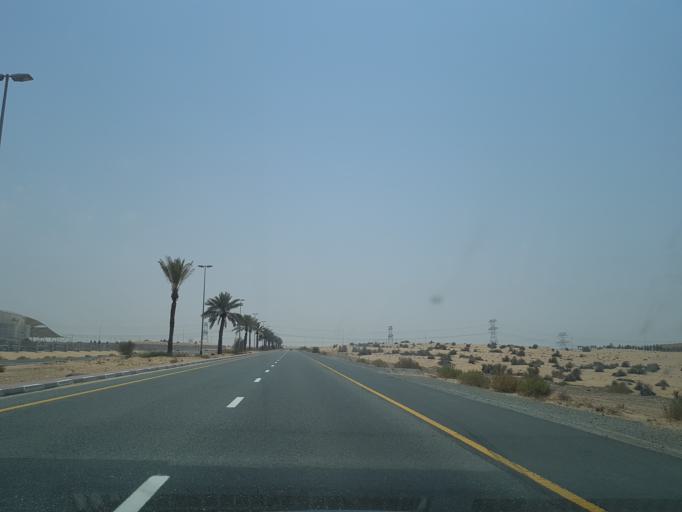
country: AE
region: Ash Shariqah
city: Sharjah
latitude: 25.1078
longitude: 55.4107
